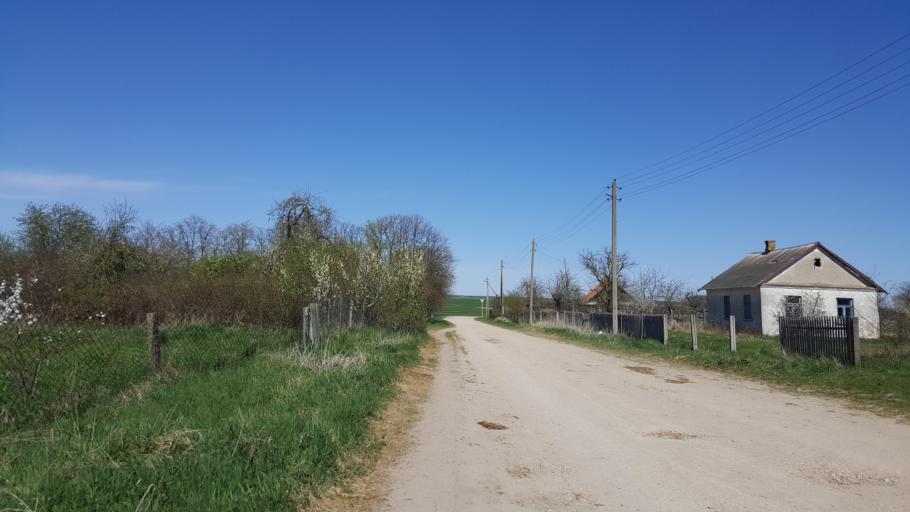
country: BY
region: Brest
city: Vysokaye
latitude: 52.3472
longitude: 23.5301
